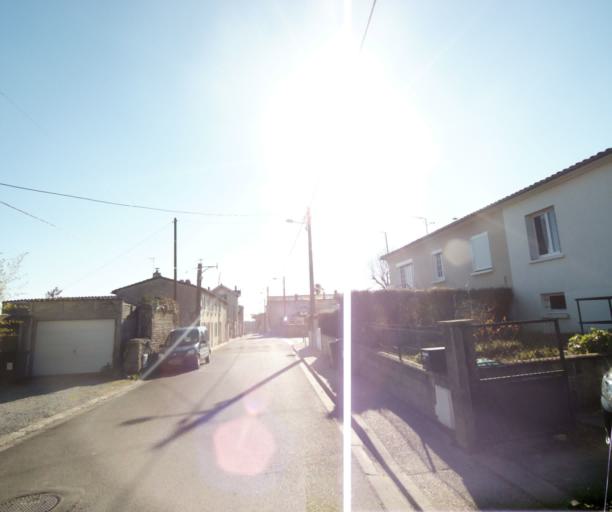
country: FR
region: Poitou-Charentes
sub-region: Departement des Deux-Sevres
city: Niort
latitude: 46.3471
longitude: -0.4715
